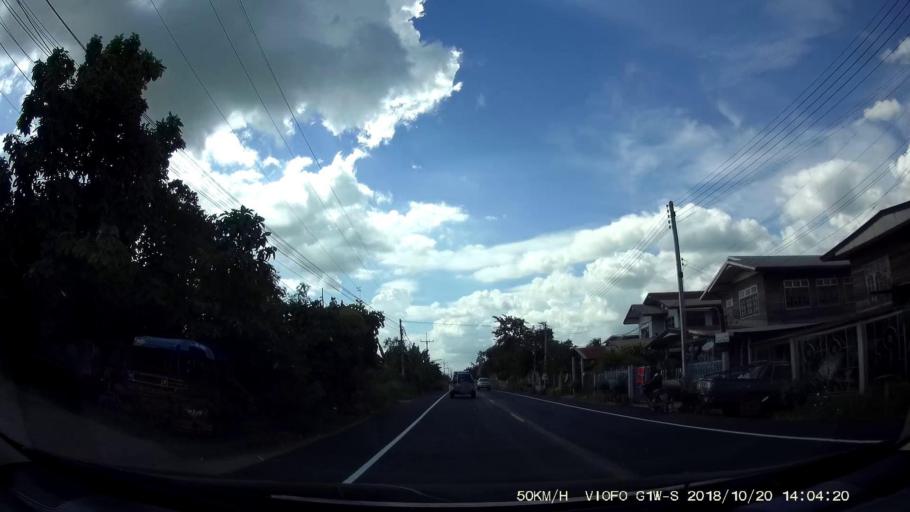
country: TH
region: Khon Kaen
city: Chum Phae
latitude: 16.4894
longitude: 102.1171
